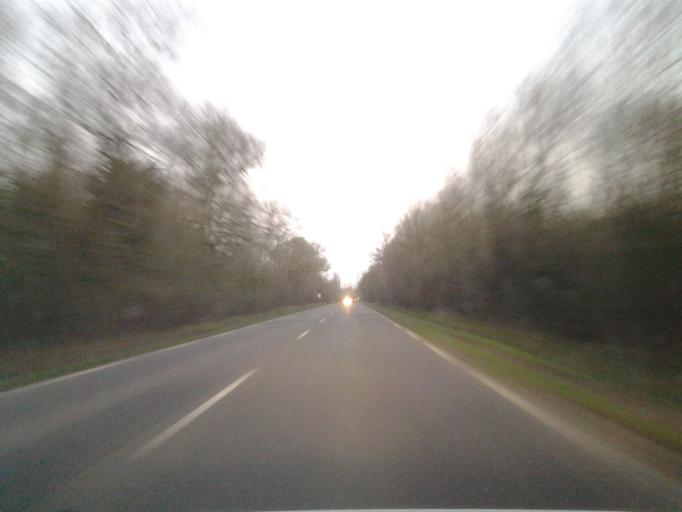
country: FR
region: Pays de la Loire
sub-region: Departement de la Vendee
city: Saint-Gervais
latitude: 46.8923
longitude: -1.9794
